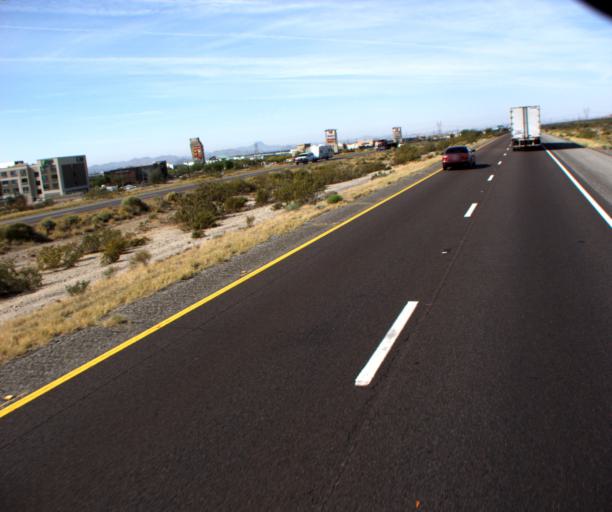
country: US
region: Arizona
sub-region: Maricopa County
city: Buckeye
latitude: 33.4458
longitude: -112.5536
